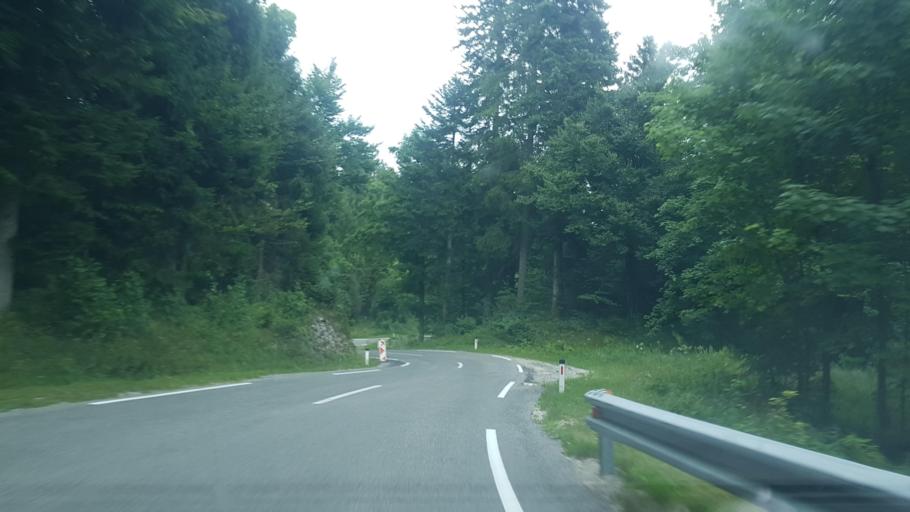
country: SI
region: Logatec
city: Logatec
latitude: 45.8751
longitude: 14.1430
